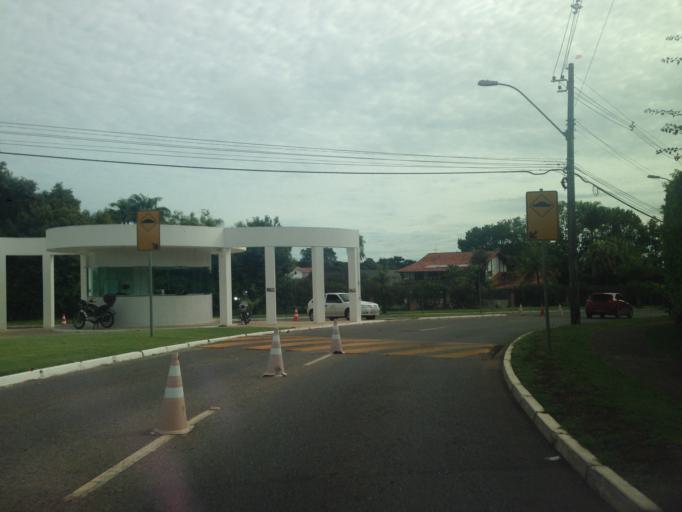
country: BR
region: Federal District
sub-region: Brasilia
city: Brasilia
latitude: -15.8342
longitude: -47.8665
